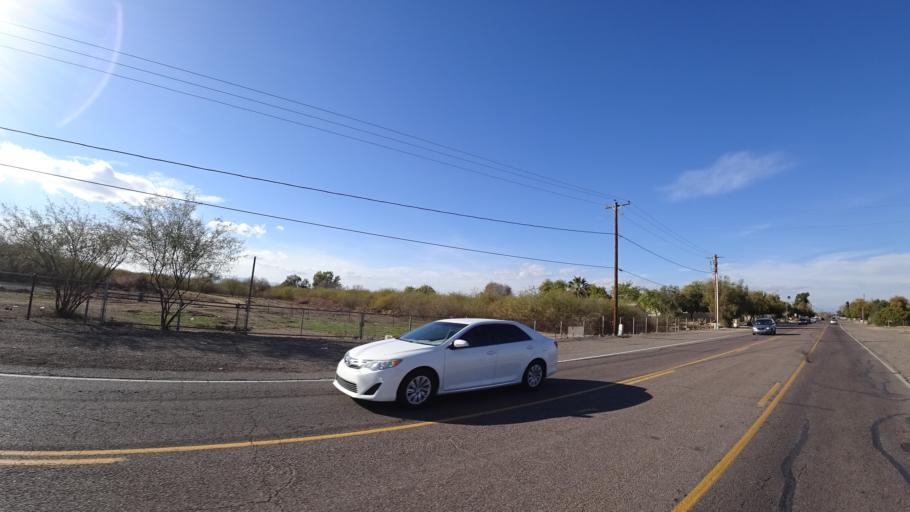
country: US
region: Arizona
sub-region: Maricopa County
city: Peoria
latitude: 33.5459
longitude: -112.2377
